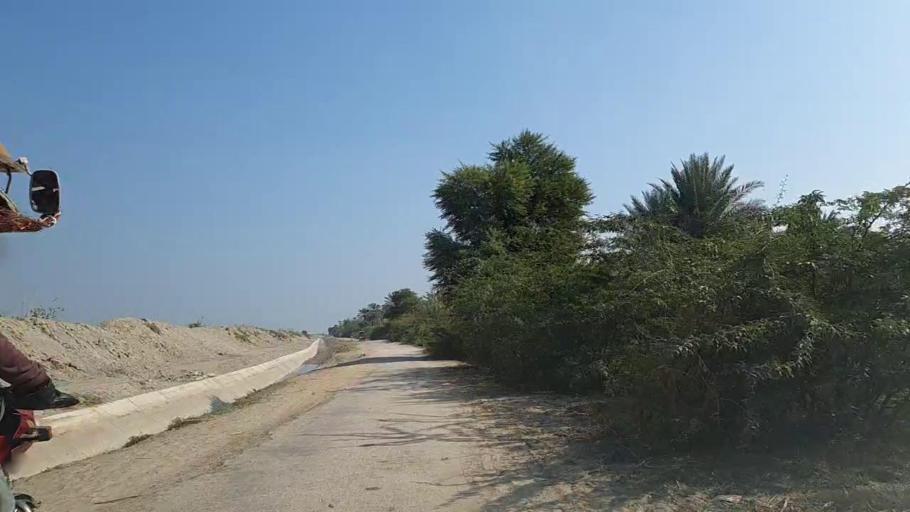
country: PK
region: Sindh
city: Jam Sahib
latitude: 26.2722
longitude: 68.5586
